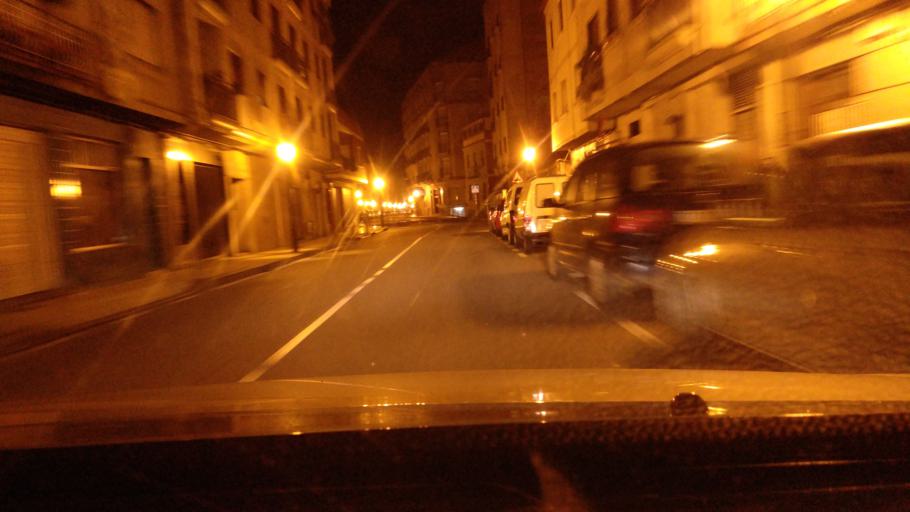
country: ES
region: Galicia
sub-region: Provincia de Pontevedra
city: Moana
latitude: 42.2824
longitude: -8.7363
